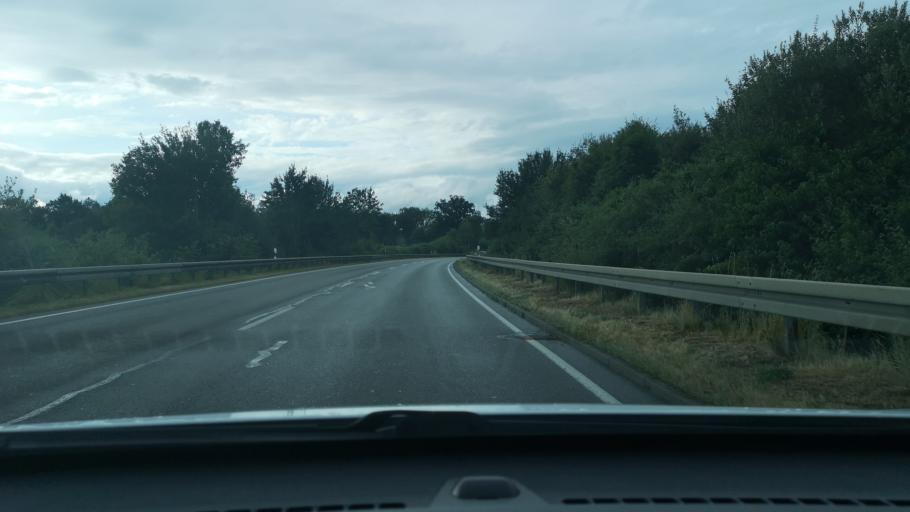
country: DE
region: Baden-Wuerttemberg
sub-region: Freiburg Region
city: Zimmern ob Rottweil
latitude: 48.1553
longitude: 8.6034
